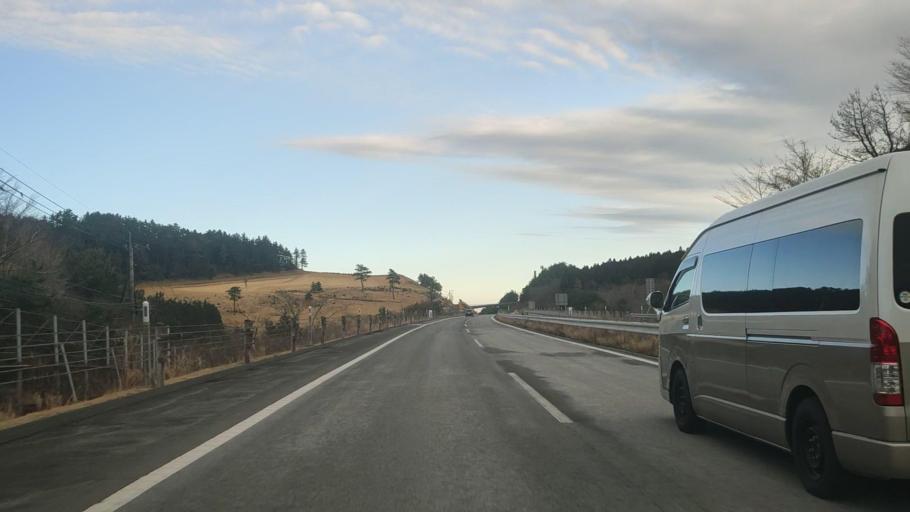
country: JP
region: Oita
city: Beppu
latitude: 33.3162
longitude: 131.4097
